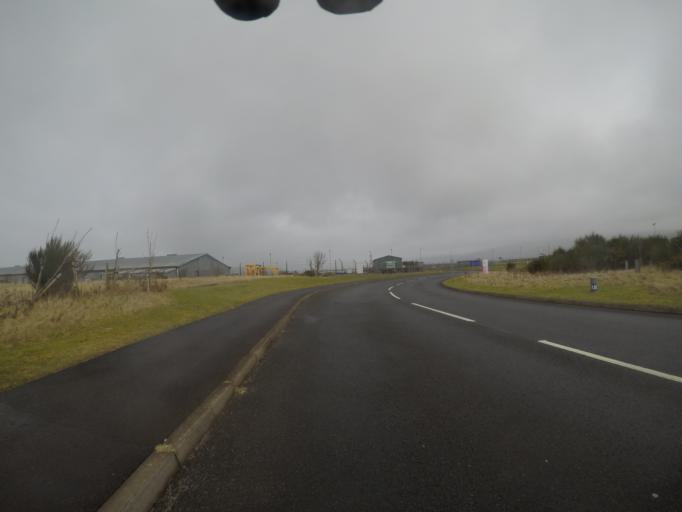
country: GB
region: Scotland
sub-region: North Ayrshire
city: Millport
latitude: 55.7224
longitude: -4.8996
